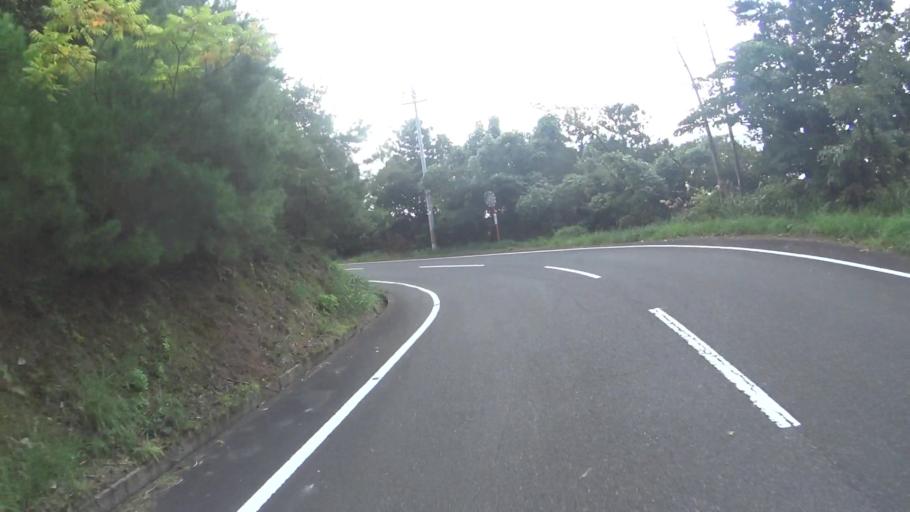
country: JP
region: Kyoto
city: Miyazu
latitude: 35.7396
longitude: 135.1750
